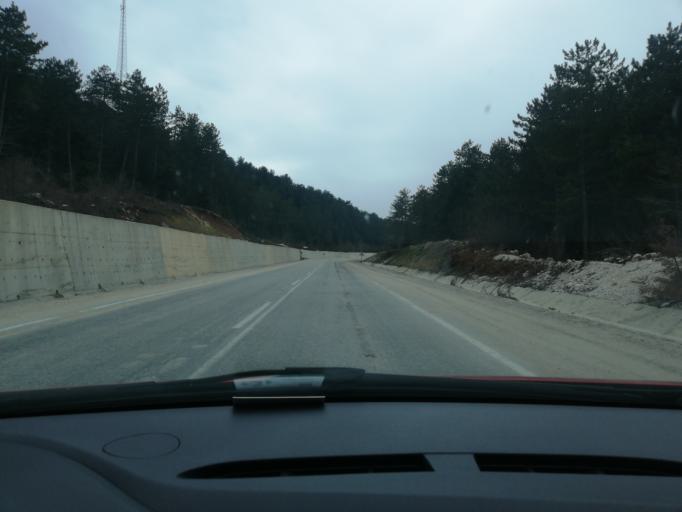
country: TR
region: Kastamonu
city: Pinarbasi
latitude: 41.5624
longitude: 33.0883
